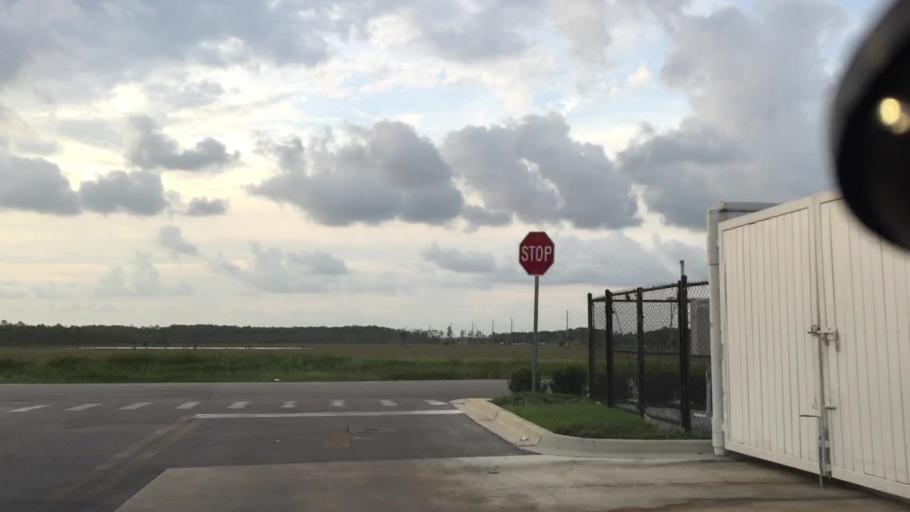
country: US
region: Florida
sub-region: Lee County
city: Gateway
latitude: 26.6182
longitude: -81.7703
